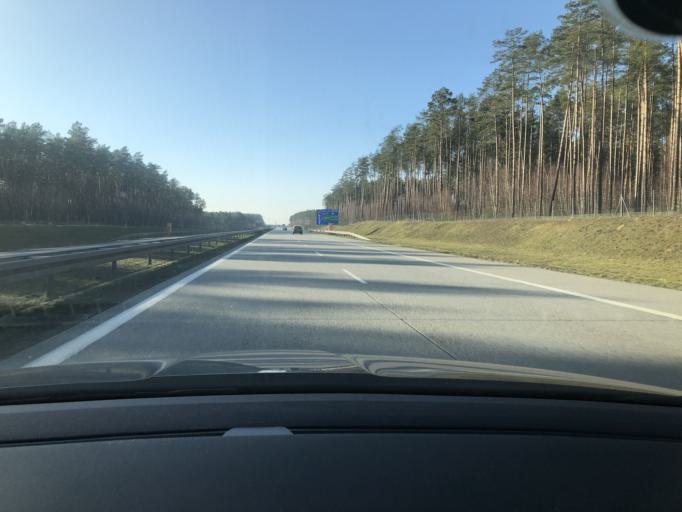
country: PL
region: Lubusz
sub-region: Powiat sulecinski
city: Torzym
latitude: 52.3260
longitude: 15.1164
